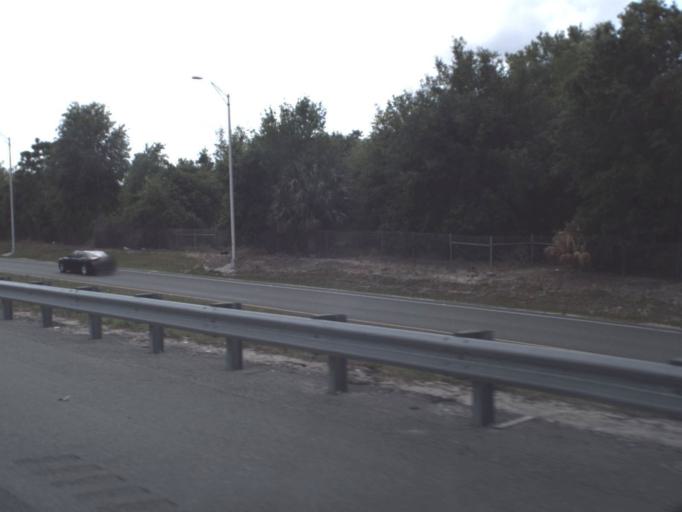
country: US
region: Florida
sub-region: Orange County
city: Paradise Heights
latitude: 28.6322
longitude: -81.5409
